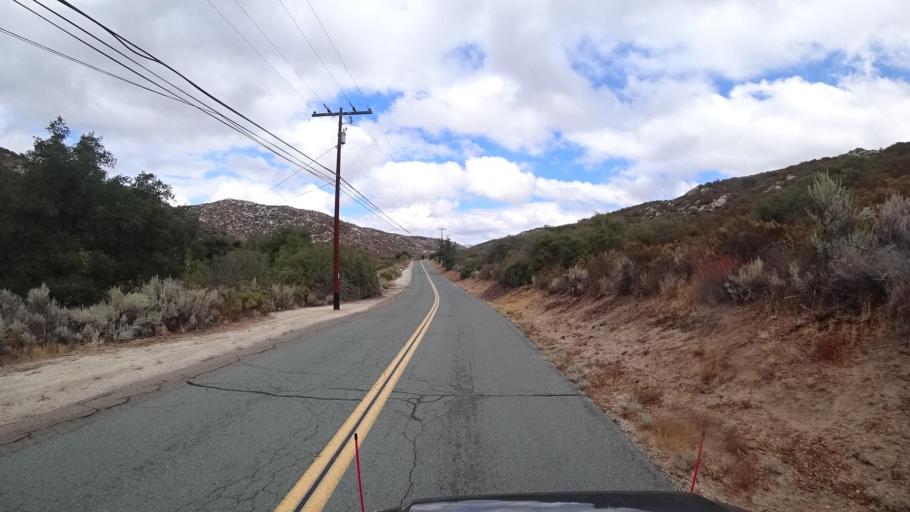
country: US
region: California
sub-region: San Diego County
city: Campo
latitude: 32.6926
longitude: -116.4320
